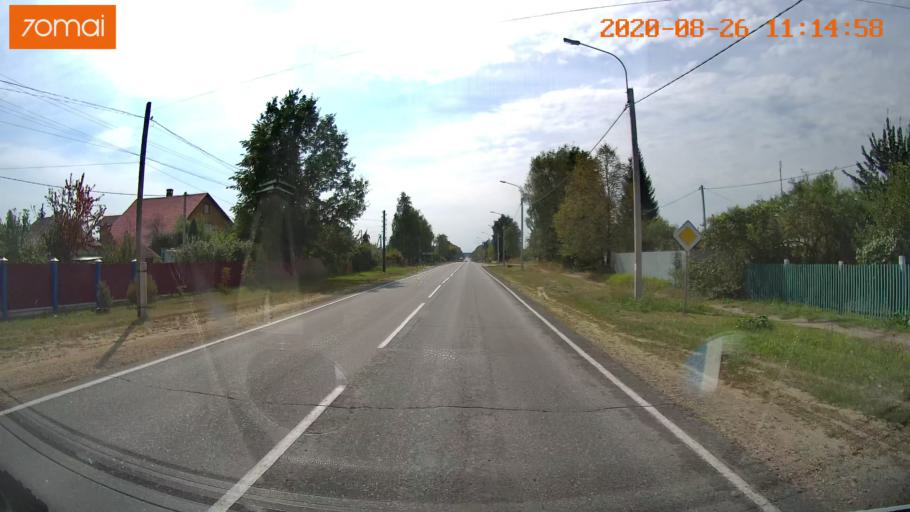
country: RU
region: Rjazan
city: Izhevskoye
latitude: 54.4439
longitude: 41.1157
